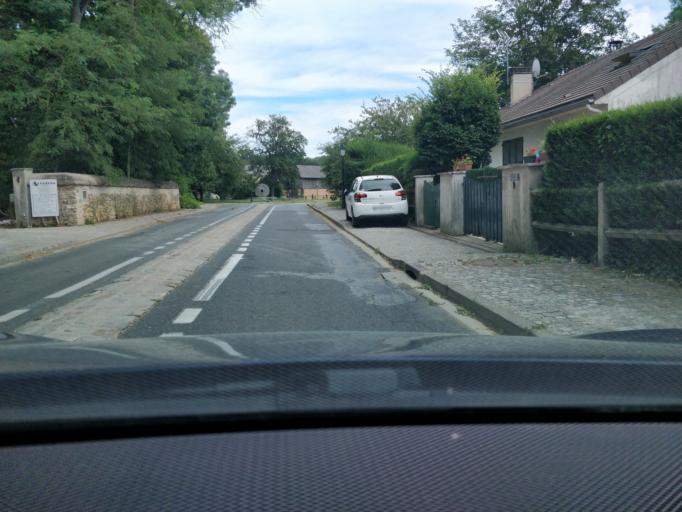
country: FR
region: Ile-de-France
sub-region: Departement de l'Essonne
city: Fontenay-les-Briis
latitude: 48.6462
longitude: 2.1516
